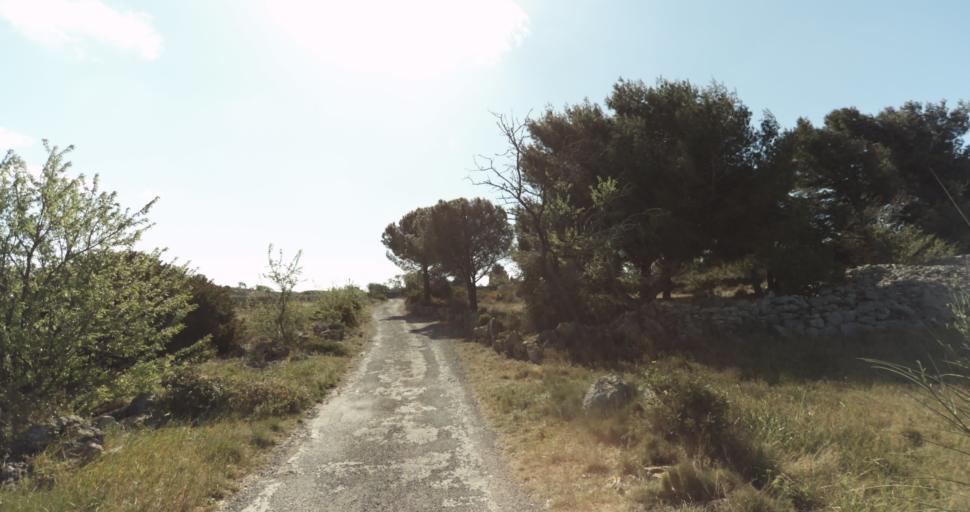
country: FR
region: Languedoc-Roussillon
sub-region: Departement de l'Aude
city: Leucate
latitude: 42.9206
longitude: 3.0267
